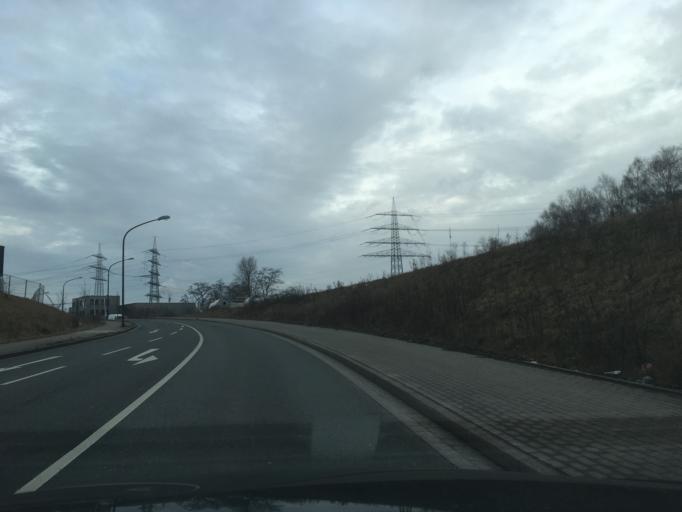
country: DE
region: North Rhine-Westphalia
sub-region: Regierungsbezirk Munster
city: Gladbeck
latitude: 51.5224
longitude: 6.9976
